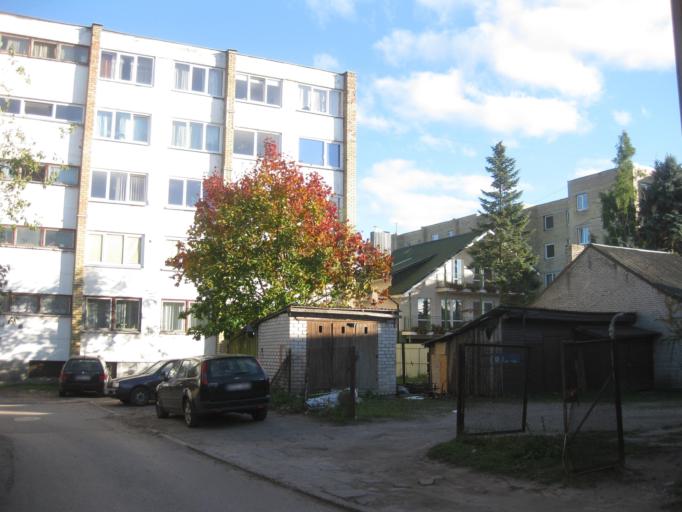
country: LT
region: Kauno apskritis
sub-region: Kaunas
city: Aleksotas
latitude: 54.8856
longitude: 23.8955
